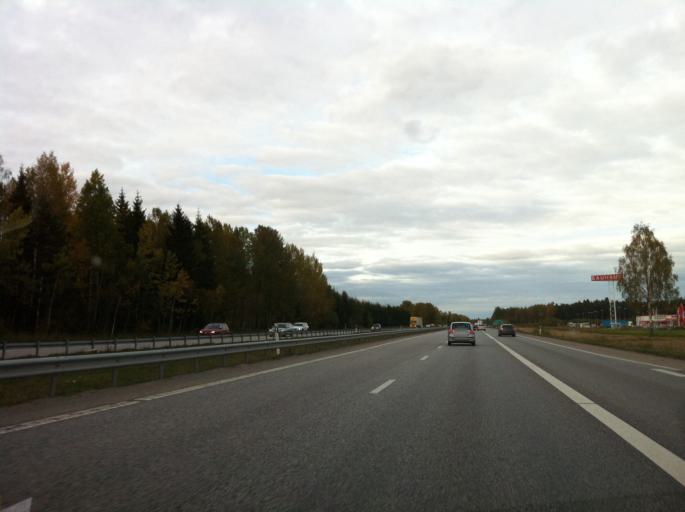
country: SE
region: OErebro
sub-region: Kumla Kommun
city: Kumla
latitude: 59.2084
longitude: 15.1288
